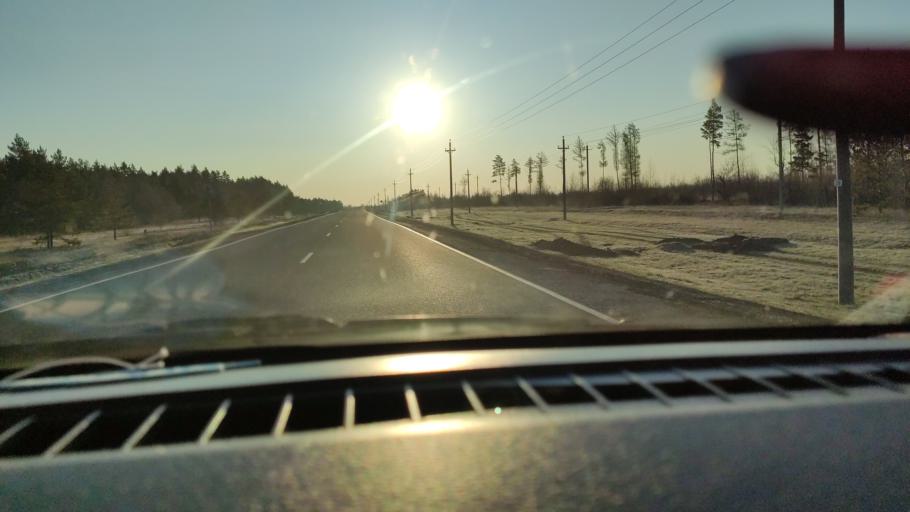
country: RU
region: Saratov
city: Sennoy
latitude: 52.1442
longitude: 46.9296
